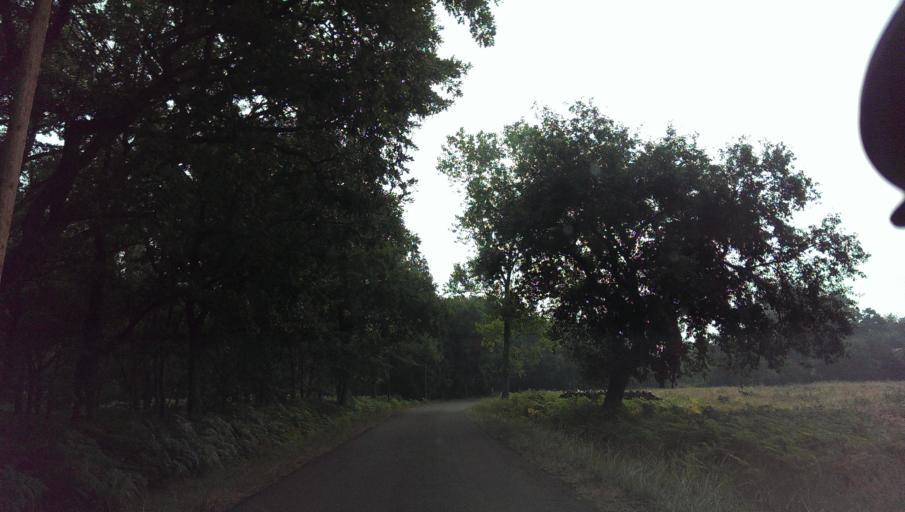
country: FR
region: Aquitaine
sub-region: Departement des Landes
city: Gabarret
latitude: 44.1116
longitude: -0.0940
